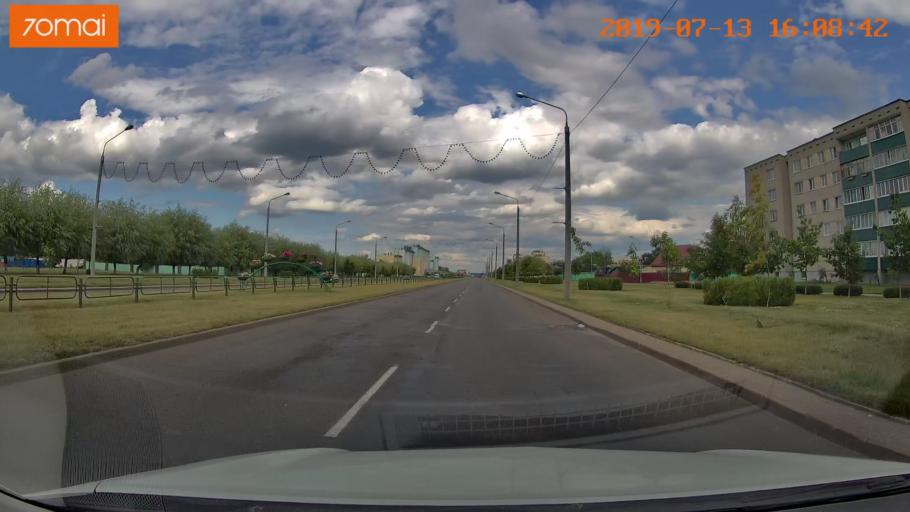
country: BY
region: Mogilev
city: Babruysk
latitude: 53.1583
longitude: 29.2202
